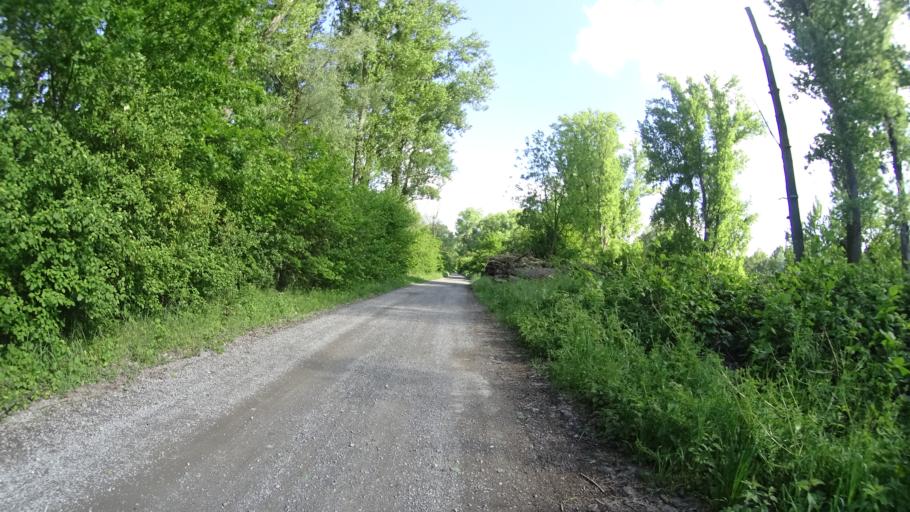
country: DE
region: Baden-Wuerttemberg
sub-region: Karlsruhe Region
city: Eggenstein-Leopoldshafen
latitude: 49.0649
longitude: 8.3467
